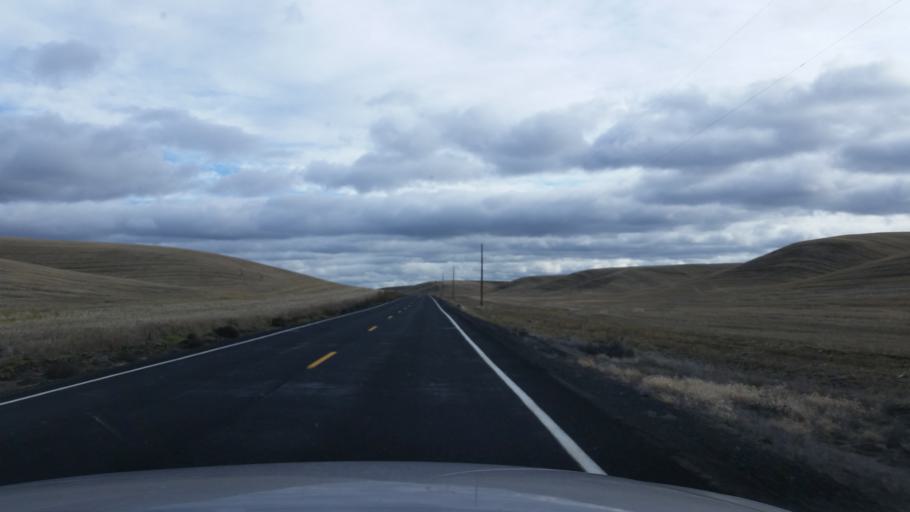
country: US
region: Washington
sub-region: Lincoln County
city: Davenport
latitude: 47.3545
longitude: -118.0336
